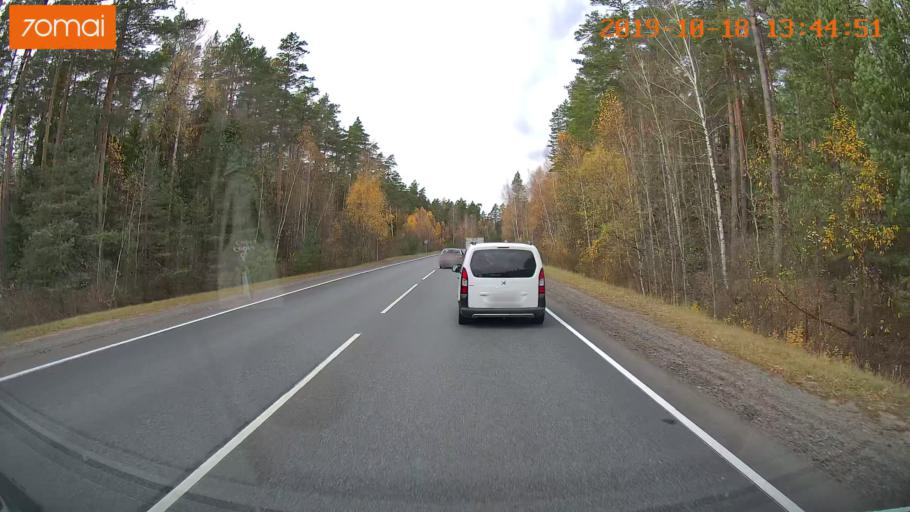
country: RU
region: Rjazan
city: Solotcha
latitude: 54.9401
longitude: 39.9548
